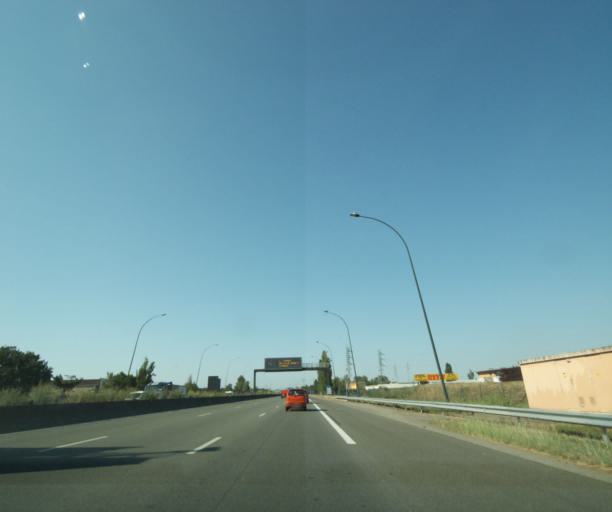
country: FR
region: Midi-Pyrenees
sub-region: Departement de la Haute-Garonne
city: Portet-sur-Garonne
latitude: 43.5437
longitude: 1.3994
